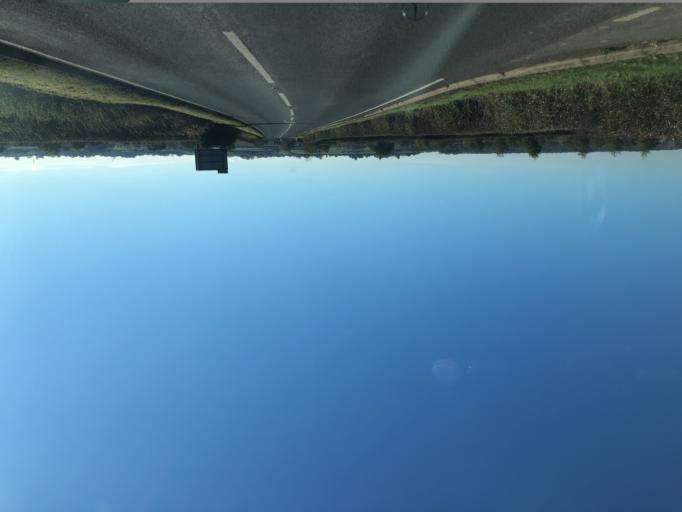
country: GB
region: England
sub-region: Warwickshire
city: Harbury
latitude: 52.2676
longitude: -1.4705
